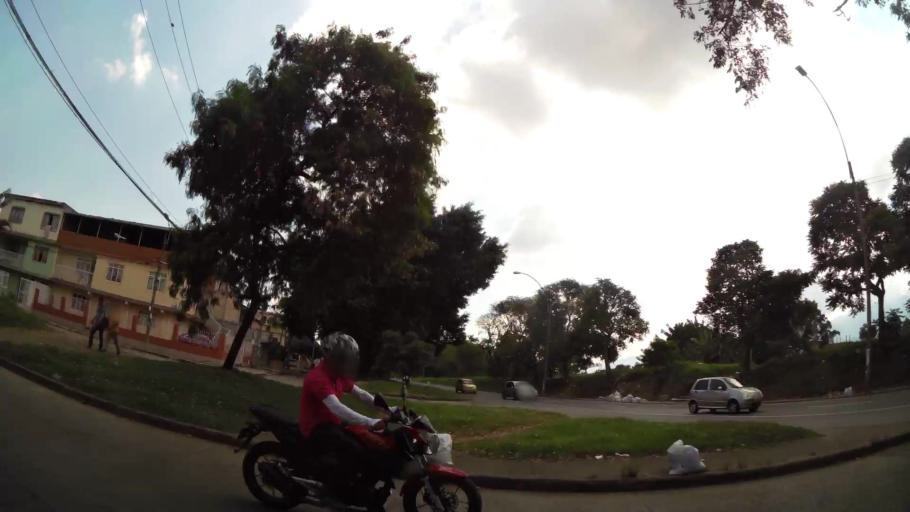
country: CO
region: Valle del Cauca
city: Cali
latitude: 3.4100
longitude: -76.5215
